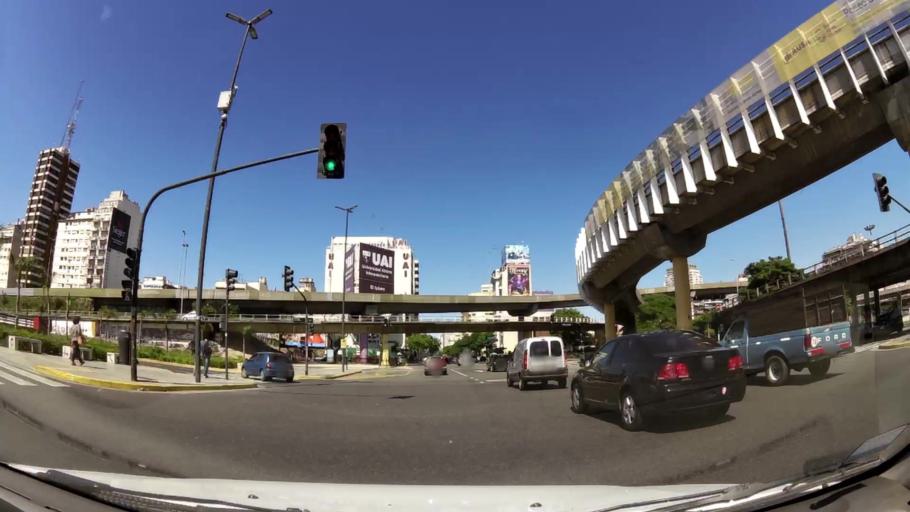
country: AR
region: Buenos Aires F.D.
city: Buenos Aires
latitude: -34.6220
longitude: -58.3810
